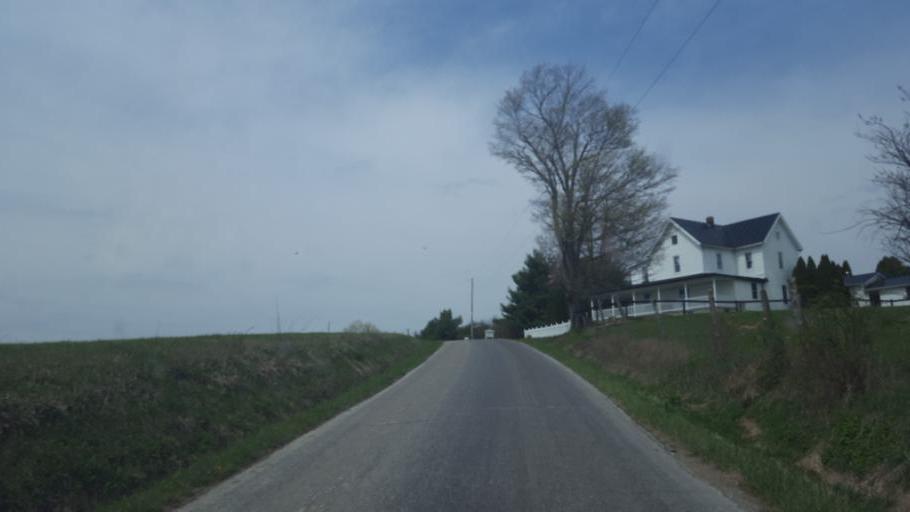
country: US
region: Ohio
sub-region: Knox County
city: Fredericktown
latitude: 40.5189
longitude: -82.6184
